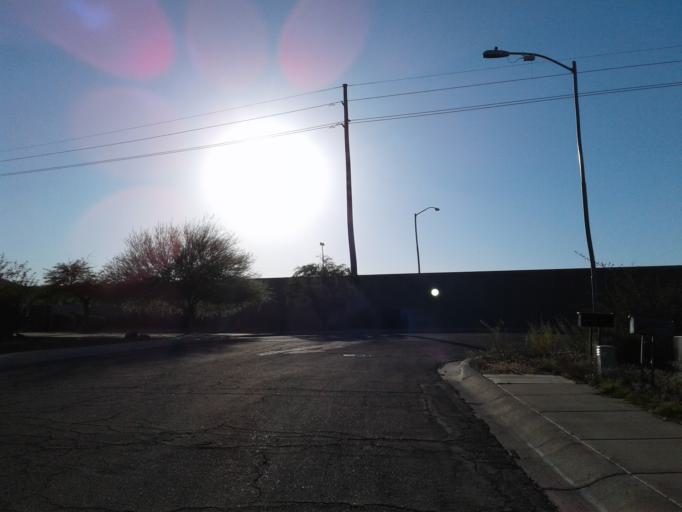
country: US
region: Arizona
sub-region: Maricopa County
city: Paradise Valley
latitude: 33.6278
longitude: -112.0075
